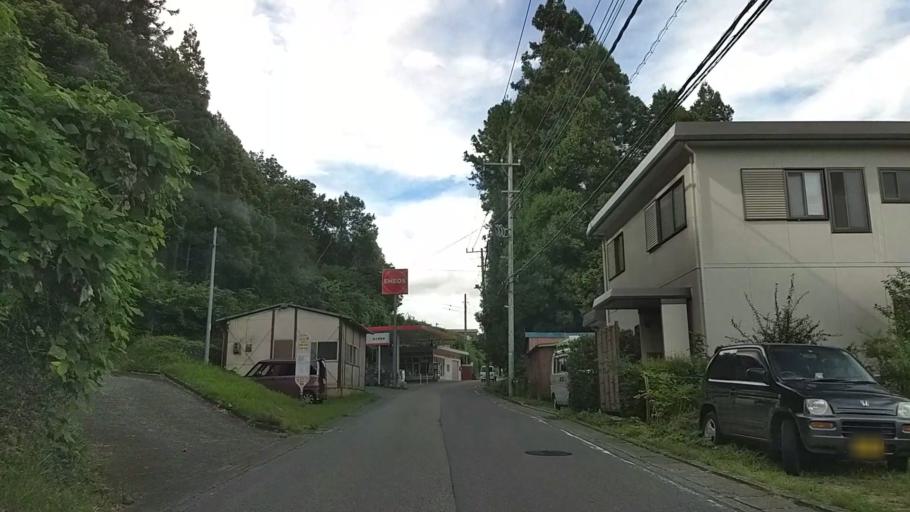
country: JP
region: Yamanashi
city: Uenohara
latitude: 35.6031
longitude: 139.1529
